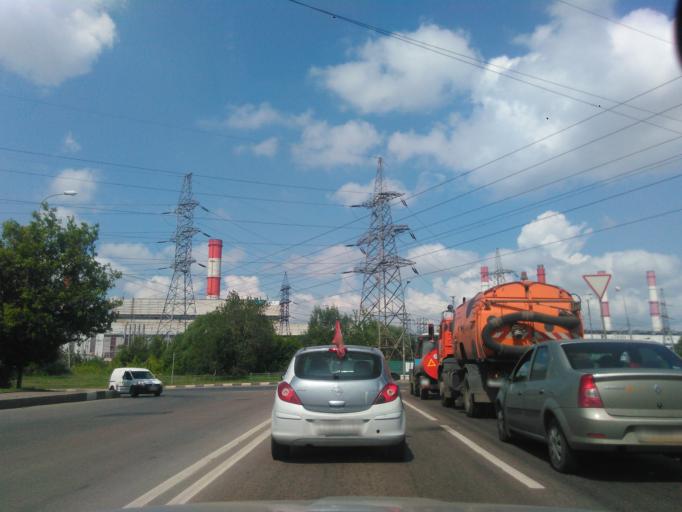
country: RU
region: Moscow
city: Businovo
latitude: 55.8889
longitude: 37.5121
